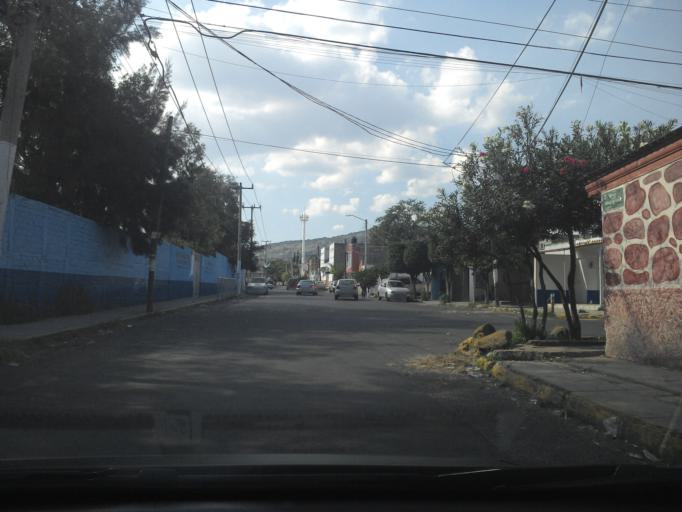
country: MX
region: Jalisco
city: Guadalajara
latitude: 20.6466
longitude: -103.4395
